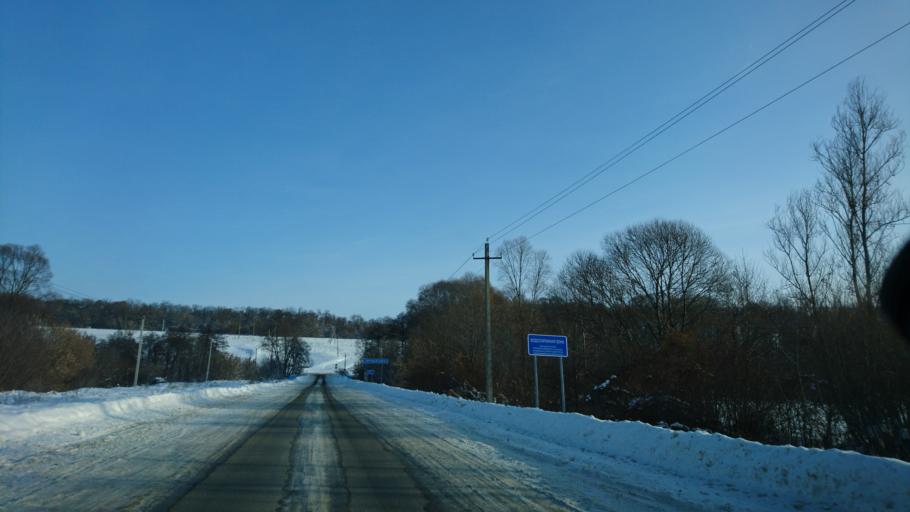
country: RU
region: Belgorod
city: Severnyy
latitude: 50.7272
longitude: 36.6090
